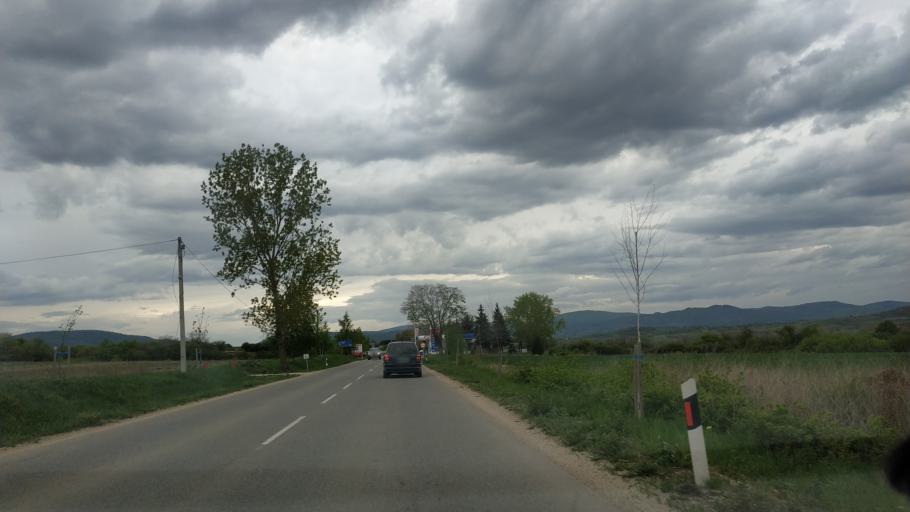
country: RS
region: Central Serbia
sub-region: Zajecarski Okrug
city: Soko Banja
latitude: 43.6527
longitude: 21.8446
